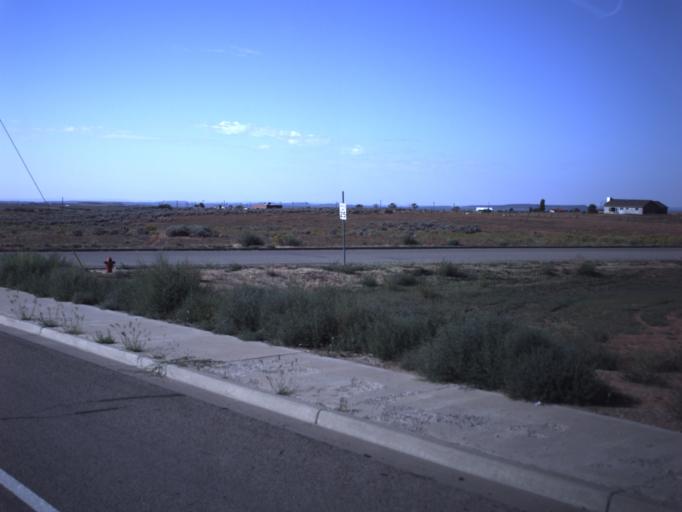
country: US
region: Utah
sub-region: San Juan County
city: Blanding
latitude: 37.6085
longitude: -109.4790
